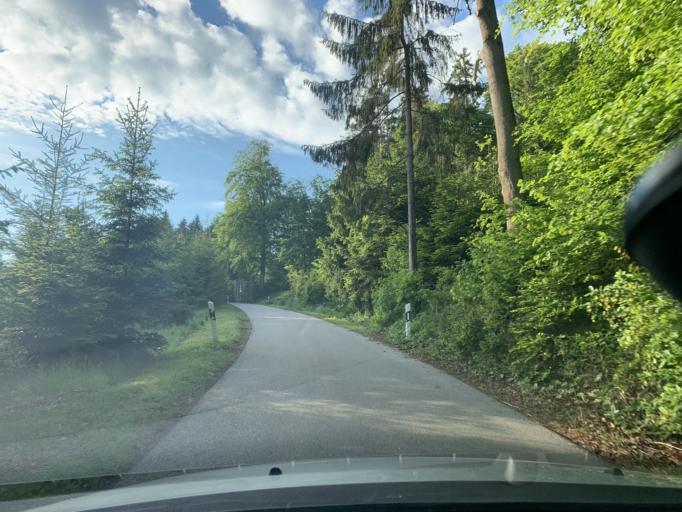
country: DE
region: Bavaria
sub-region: Lower Bavaria
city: Stallwang
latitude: 48.5197
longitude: 12.2135
